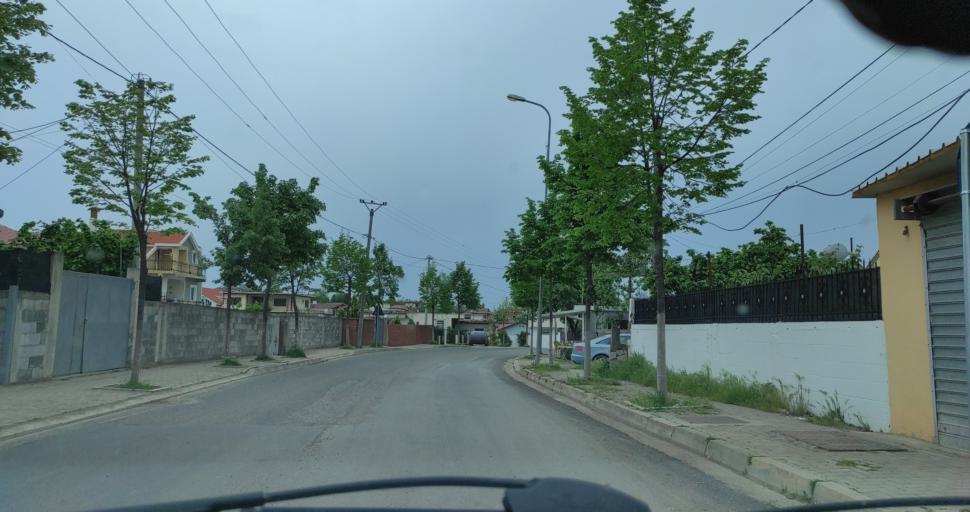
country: AL
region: Lezhe
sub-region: Rrethi i Kurbinit
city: Mamurras
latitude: 41.5815
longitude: 19.6918
